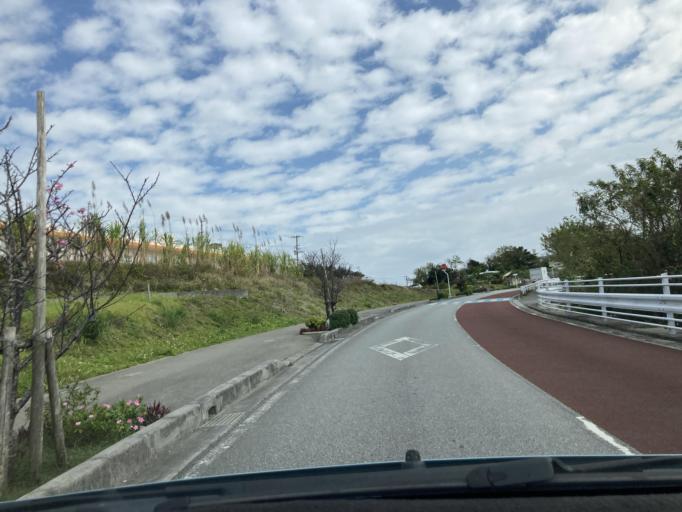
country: JP
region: Okinawa
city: Tomigusuku
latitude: 26.1861
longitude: 127.6912
